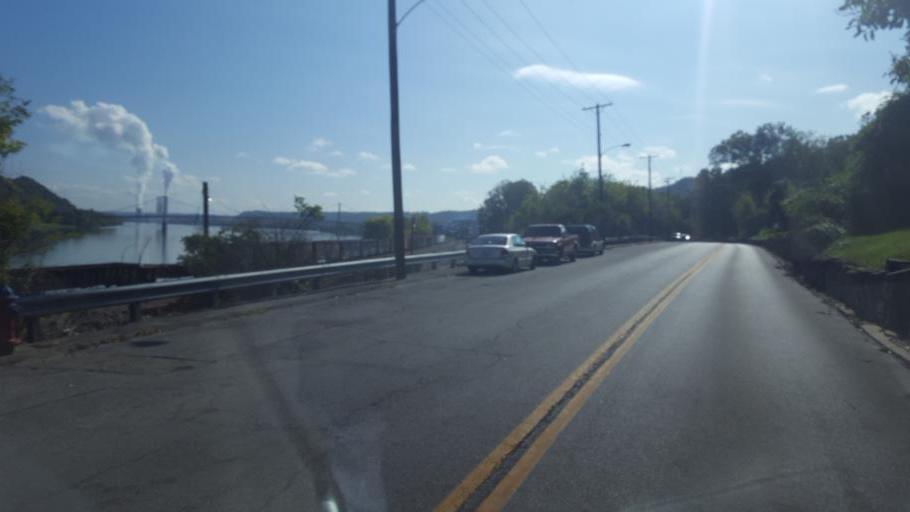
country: US
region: Ohio
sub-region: Brown County
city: Aberdeen
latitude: 38.6546
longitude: -83.7746
